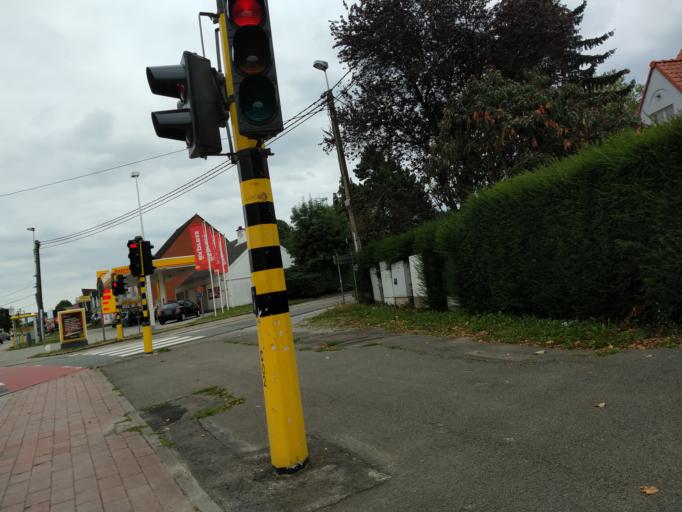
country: BE
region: Flanders
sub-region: Provincie Vlaams-Brabant
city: Hoeilaart
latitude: 50.7869
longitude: 4.4978
